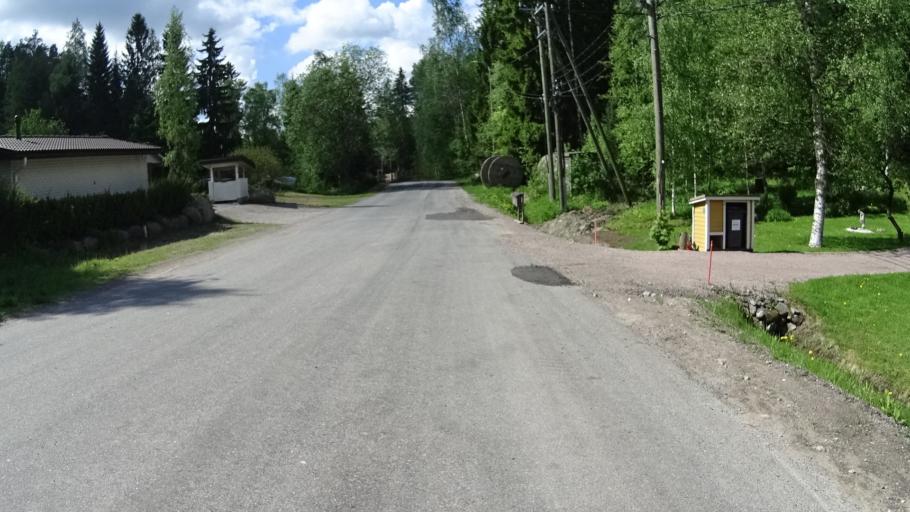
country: FI
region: Uusimaa
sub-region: Helsinki
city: Espoo
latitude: 60.2251
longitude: 24.6299
